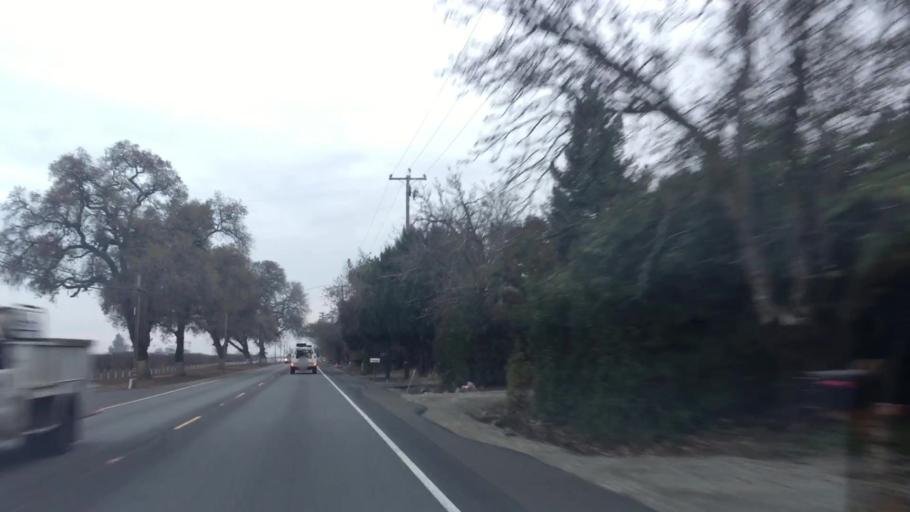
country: US
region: California
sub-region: Sutter County
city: Live Oak
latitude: 39.2486
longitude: -121.5994
